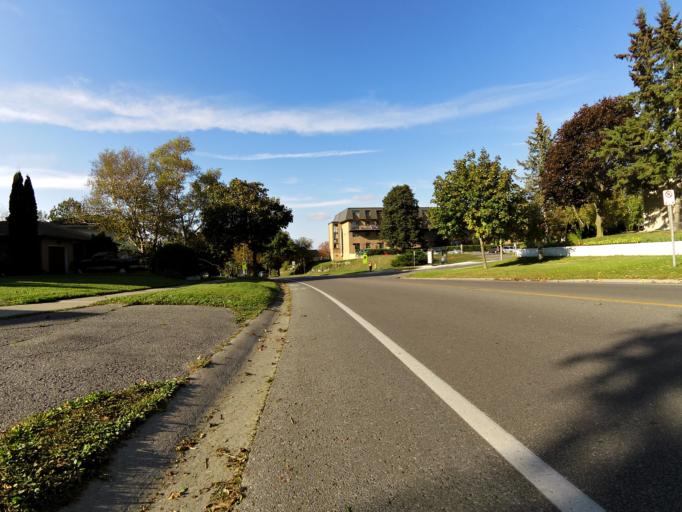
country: CA
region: Ontario
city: Kingston
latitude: 44.2341
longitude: -76.5331
